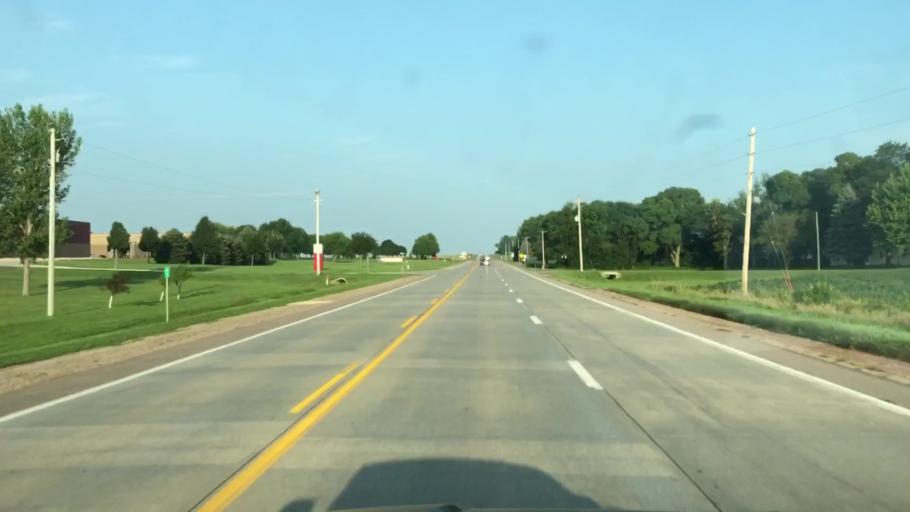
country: US
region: Iowa
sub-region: O'Brien County
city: Sheldon
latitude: 43.1859
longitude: -95.8757
